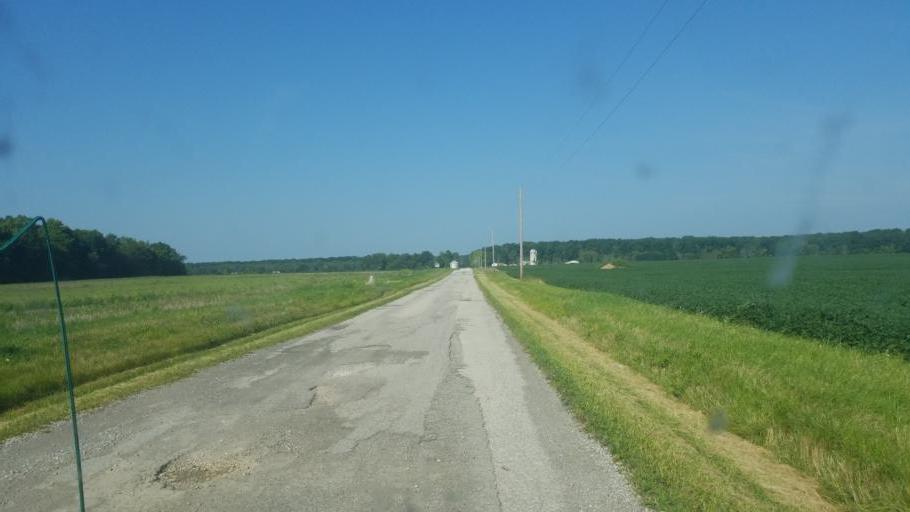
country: US
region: Ohio
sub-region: Lorain County
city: Wellington
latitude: 41.1306
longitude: -82.1837
